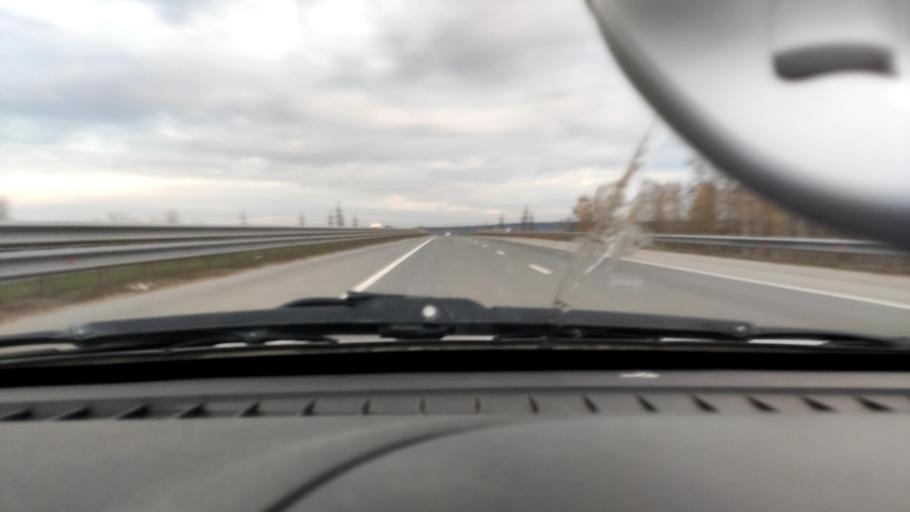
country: RU
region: Perm
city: Froly
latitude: 57.9311
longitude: 56.2940
